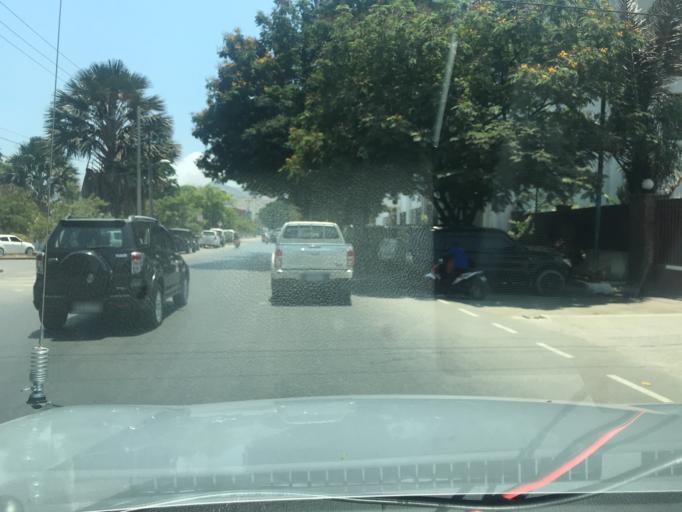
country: TL
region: Dili
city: Dili
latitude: -8.5541
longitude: 125.5727
